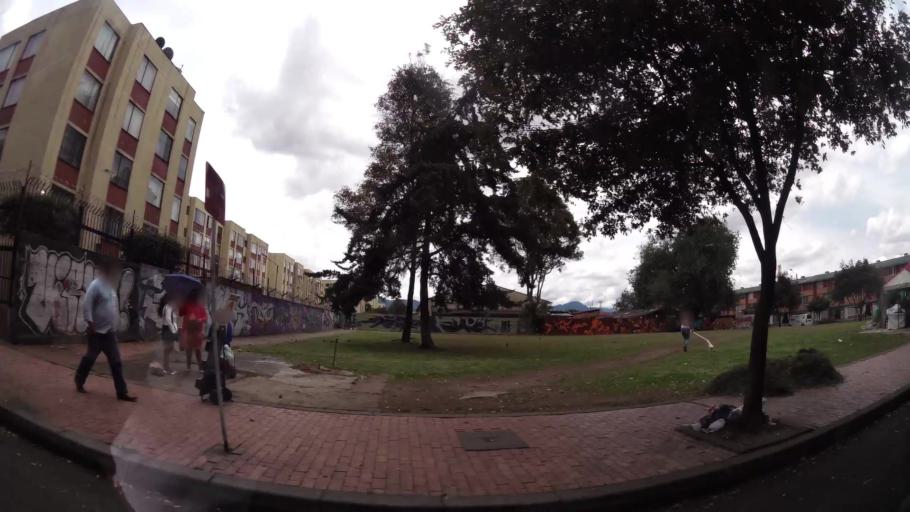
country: CO
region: Cundinamarca
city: Funza
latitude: 4.7013
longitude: -74.1173
